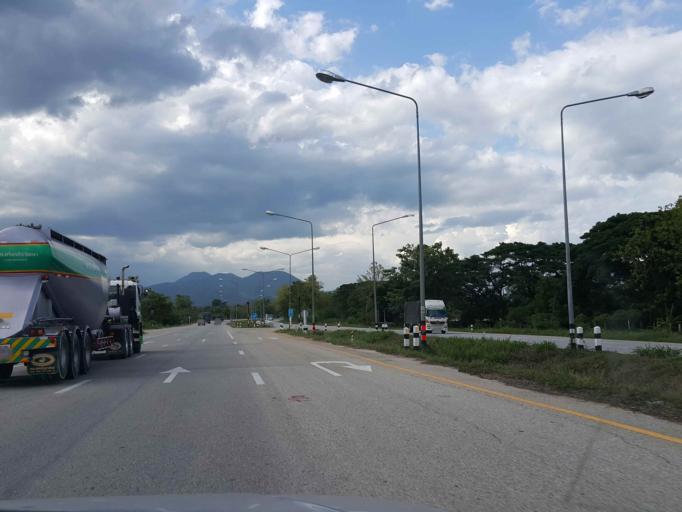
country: TH
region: Lampang
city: Thoen
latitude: 17.7172
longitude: 99.2290
